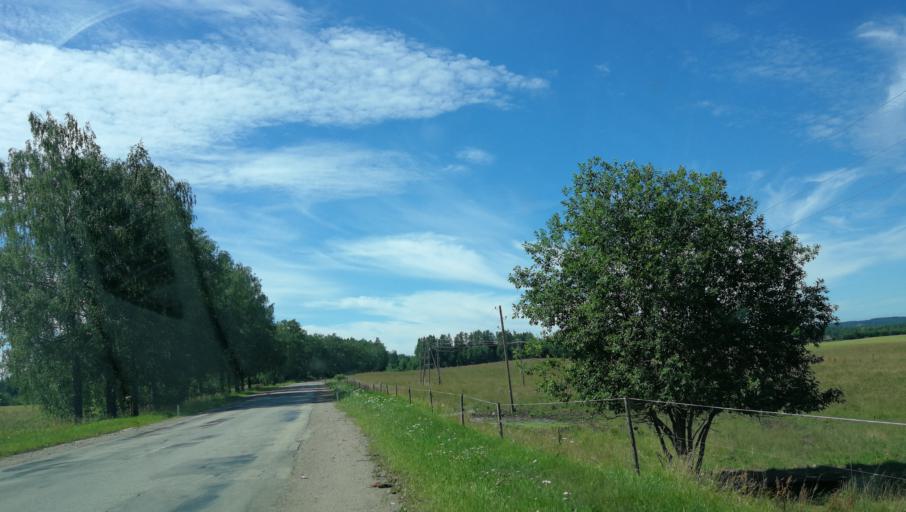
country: LV
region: Cesvaine
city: Cesvaine
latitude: 57.0045
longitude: 26.4021
